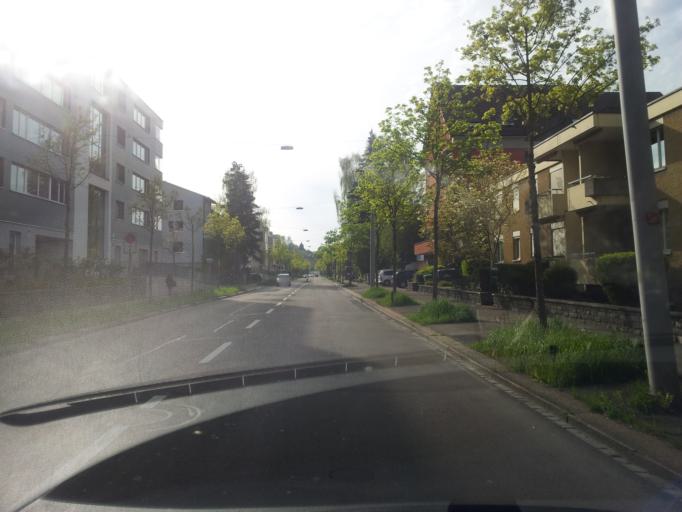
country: CH
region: Zurich
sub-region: Bezirk Zuerich
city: Zuerich (Kreis 11) / Oerlikon
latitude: 47.4101
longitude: 8.5344
